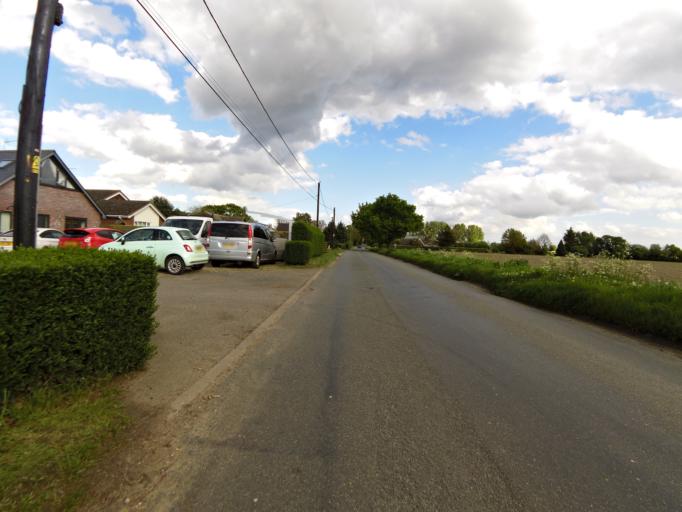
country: GB
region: England
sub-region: Suffolk
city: Woolpit
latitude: 52.2145
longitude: 0.9066
